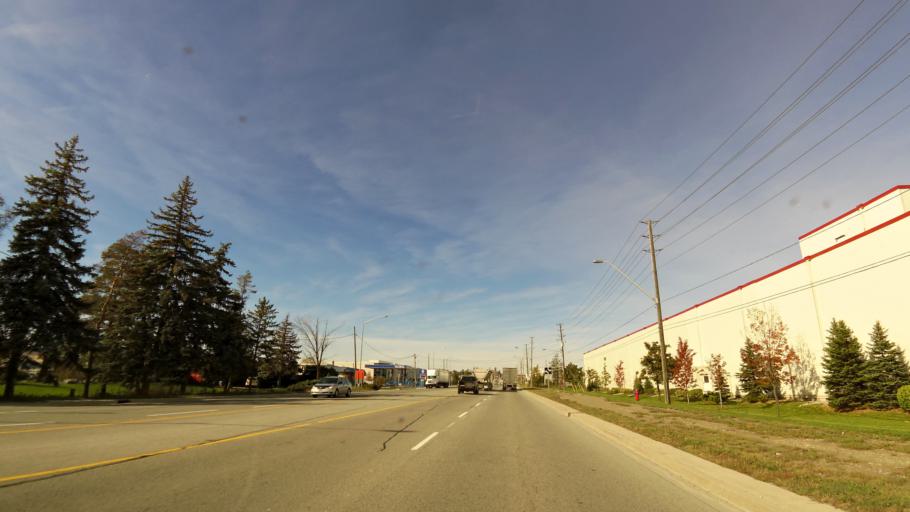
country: CA
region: Ontario
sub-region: Halton
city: Milton
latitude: 43.5352
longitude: -79.9149
